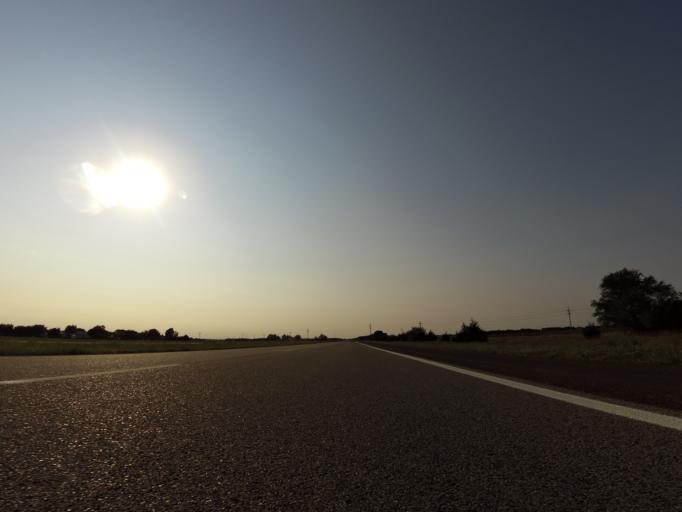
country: US
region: Kansas
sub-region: Reno County
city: South Hutchinson
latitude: 37.9537
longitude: -97.8990
